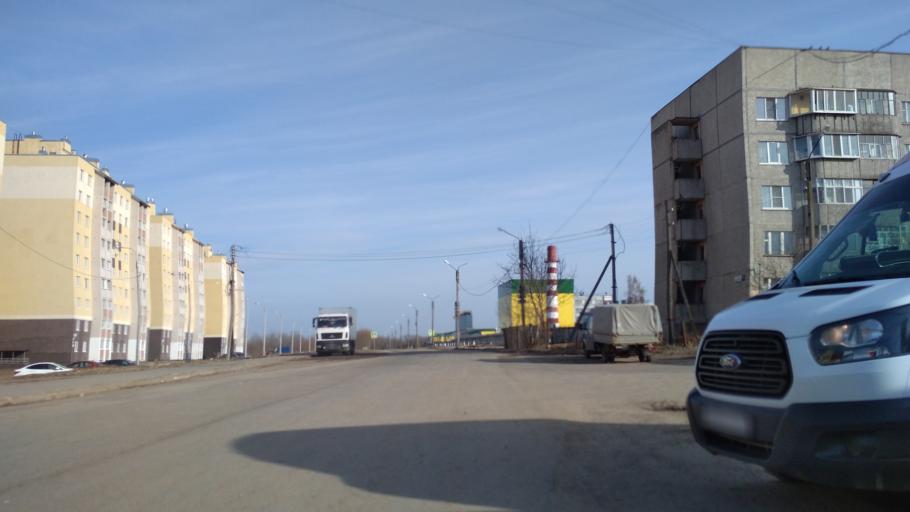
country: RU
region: Chuvashia
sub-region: Cheboksarskiy Rayon
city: Cheboksary
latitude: 56.1375
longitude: 47.3093
